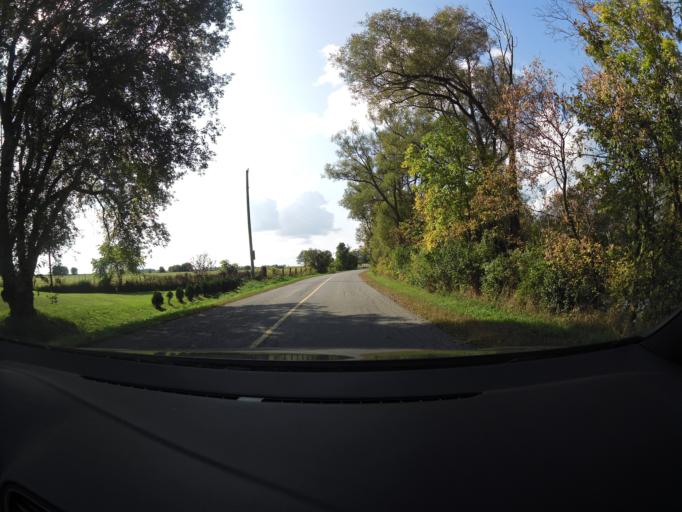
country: CA
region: Ontario
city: Arnprior
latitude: 45.3943
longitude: -76.1923
